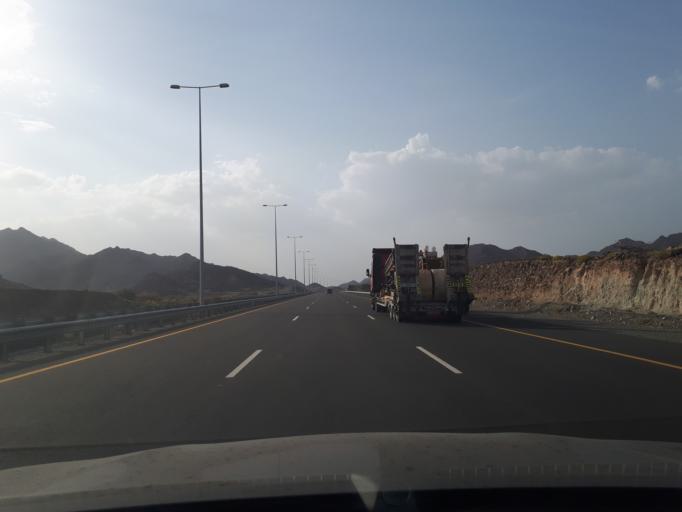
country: OM
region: Ash Sharqiyah
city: Ibra'
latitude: 22.8556
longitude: 58.3128
